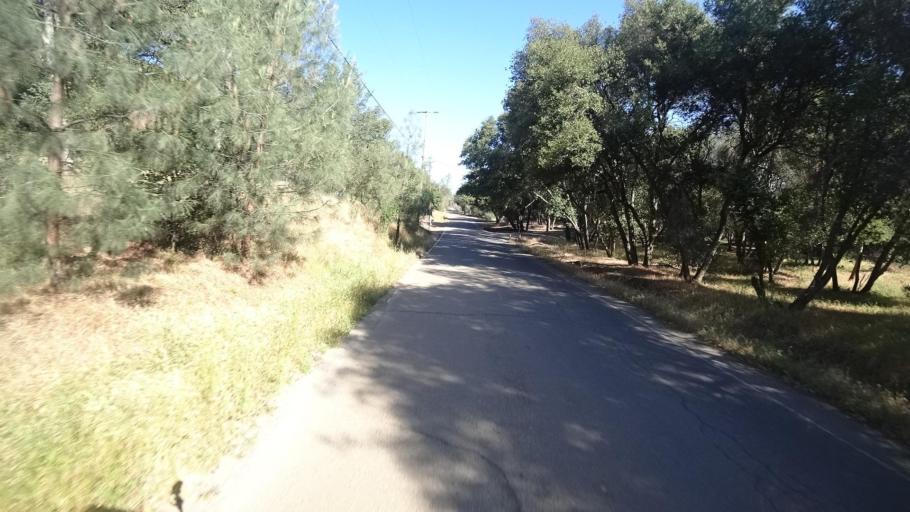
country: US
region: California
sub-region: Lake County
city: Clearlake
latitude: 38.9747
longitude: -122.6665
